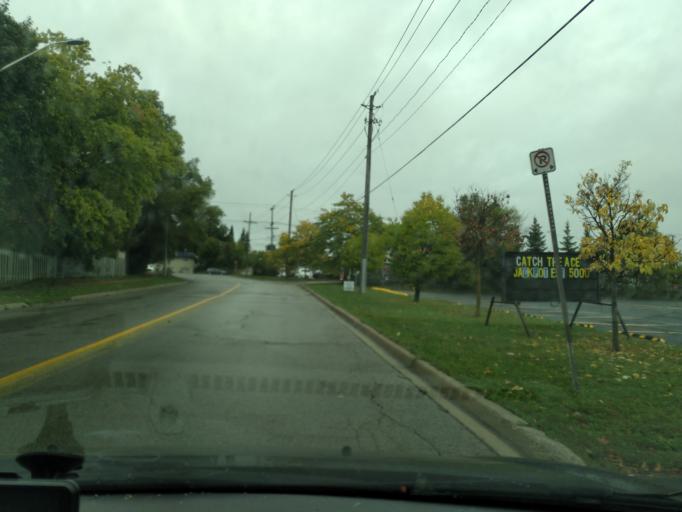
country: CA
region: Ontario
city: Barrie
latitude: 44.4100
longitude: -79.6893
